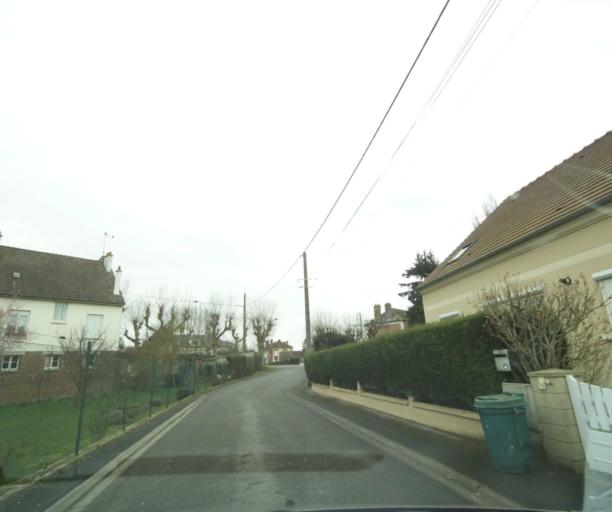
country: FR
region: Picardie
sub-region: Departement de l'Oise
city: Noyon
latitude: 49.5828
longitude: 2.9954
